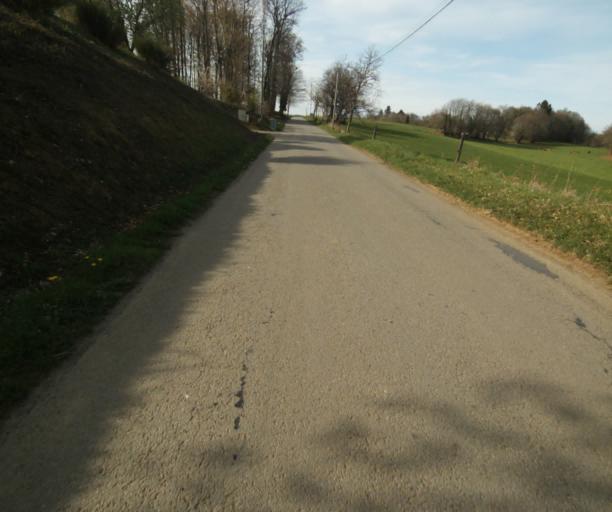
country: FR
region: Limousin
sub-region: Departement de la Correze
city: Naves
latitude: 45.2992
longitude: 1.7394
